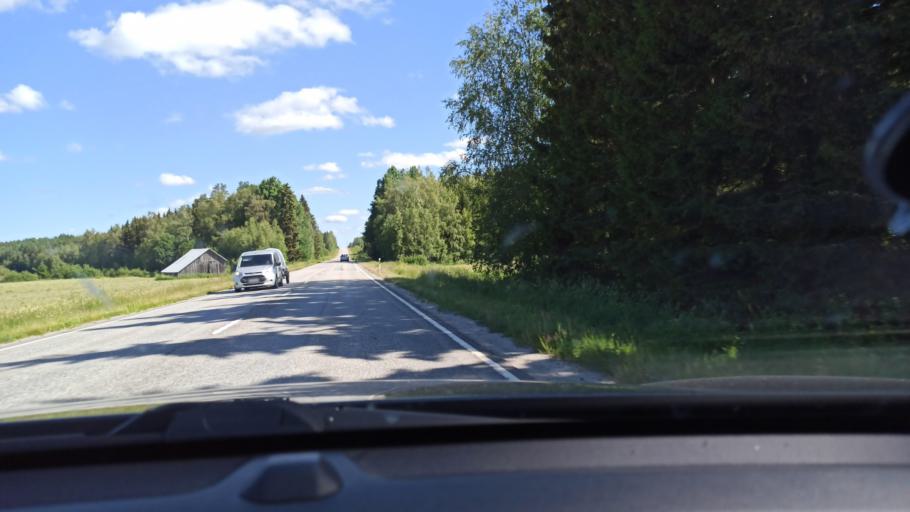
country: FI
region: Ostrobothnia
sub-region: Vaasa
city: Malax
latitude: 62.9914
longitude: 21.6471
